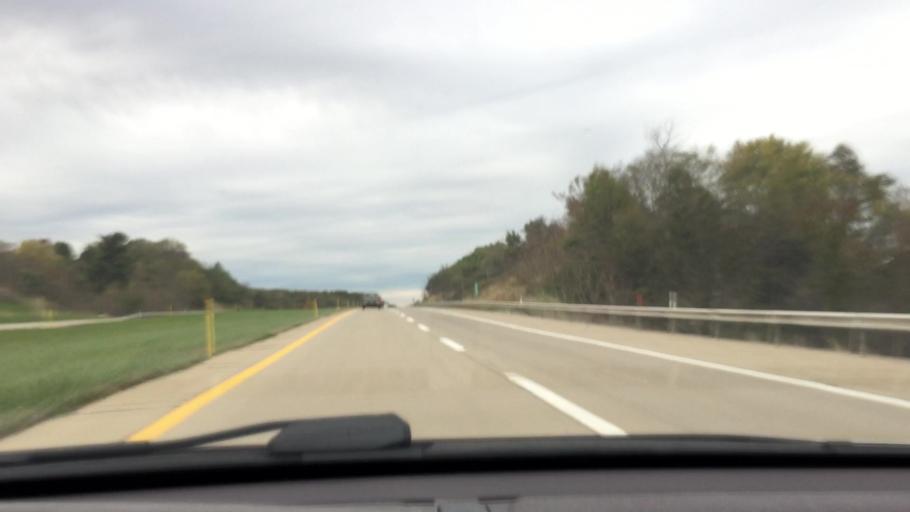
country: US
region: Pennsylvania
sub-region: Lawrence County
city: New Beaver
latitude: 40.8546
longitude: -80.3687
